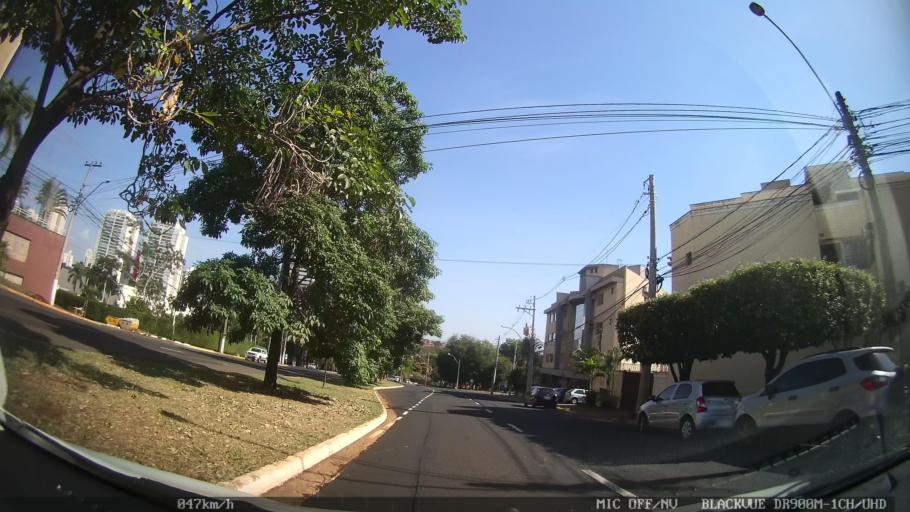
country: BR
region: Sao Paulo
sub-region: Ribeirao Preto
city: Ribeirao Preto
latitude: -21.2112
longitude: -47.8181
